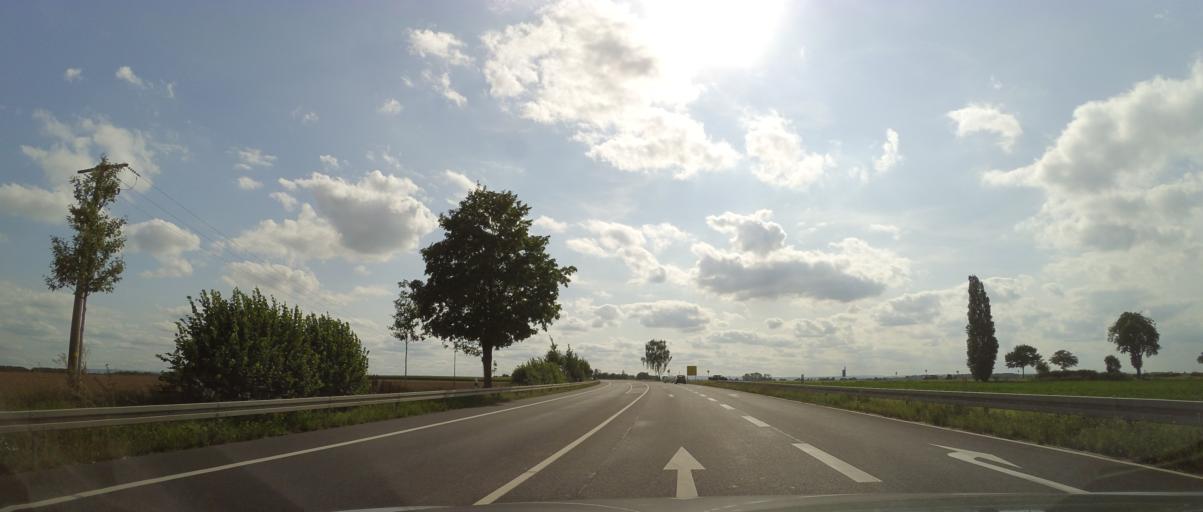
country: DE
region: North Rhine-Westphalia
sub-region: Regierungsbezirk Koln
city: Norvenich
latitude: 50.7591
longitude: 6.7207
